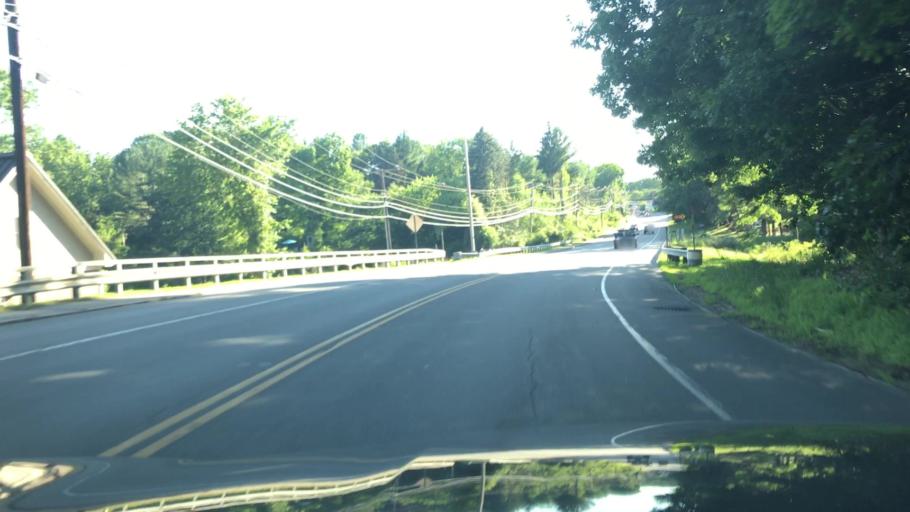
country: US
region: New Hampshire
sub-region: Strafford County
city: Durham
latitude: 43.1357
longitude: -70.9130
